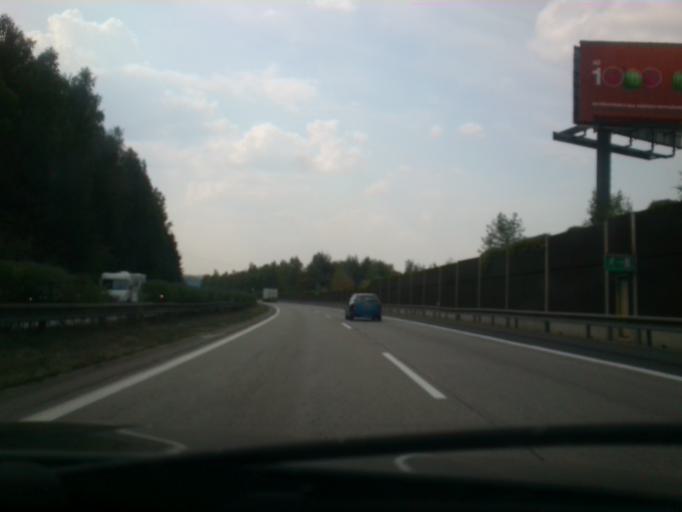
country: CZ
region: Central Bohemia
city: Ondrejov
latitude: 49.8683
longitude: 14.7807
